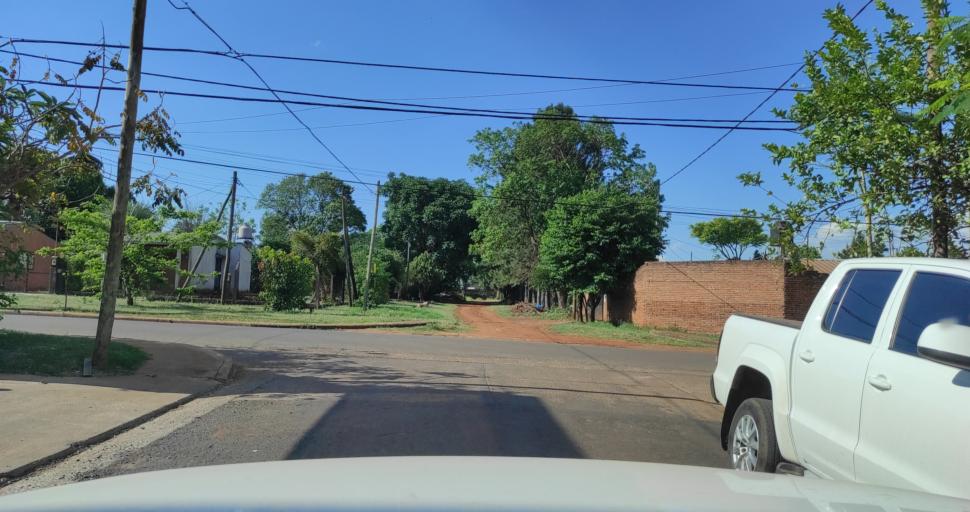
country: AR
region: Misiones
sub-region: Departamento de Capital
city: Posadas
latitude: -27.4129
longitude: -55.9256
